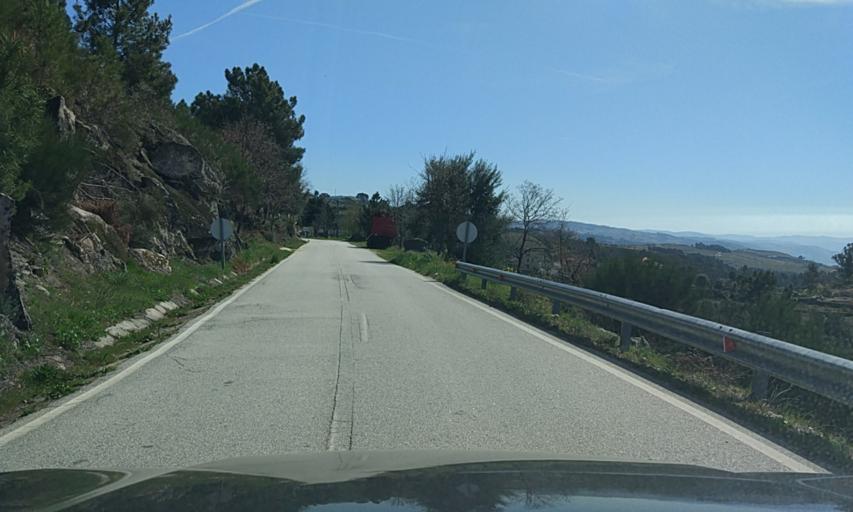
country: PT
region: Vila Real
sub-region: Sabrosa
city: Sabrosa
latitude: 41.3363
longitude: -7.5794
